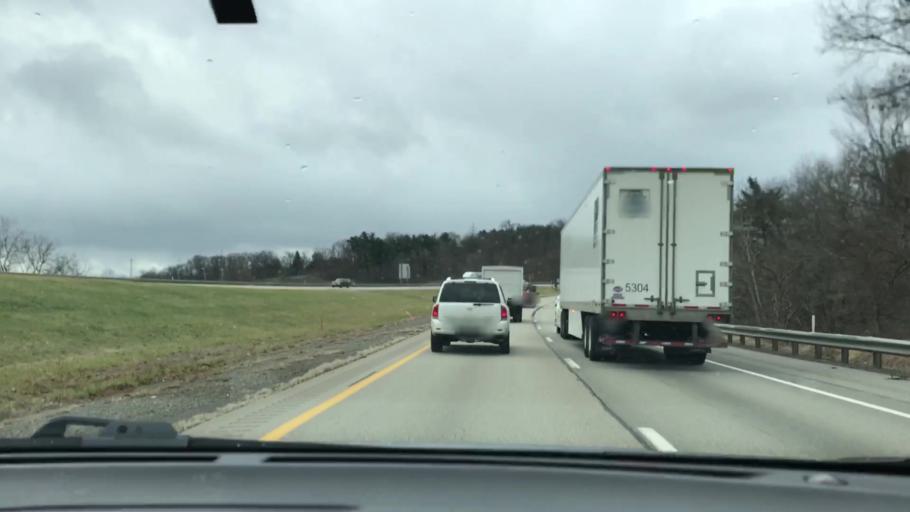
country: US
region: Pennsylvania
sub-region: Allegheny County
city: Franklin Park
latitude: 40.5861
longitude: -80.1010
